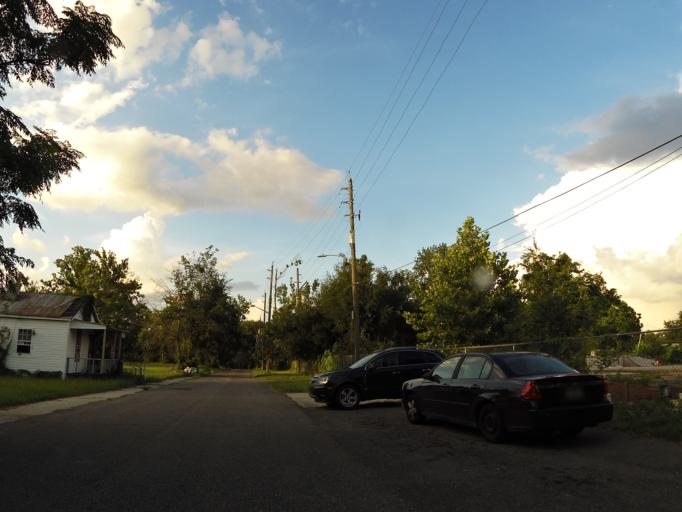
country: US
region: Florida
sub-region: Duval County
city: Jacksonville
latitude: 30.3260
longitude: -81.6842
